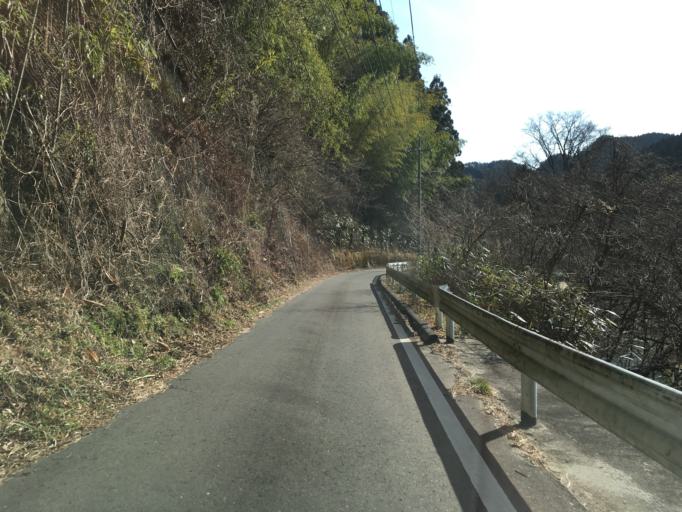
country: JP
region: Ibaraki
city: Kitaibaraki
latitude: 36.7955
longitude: 140.6533
